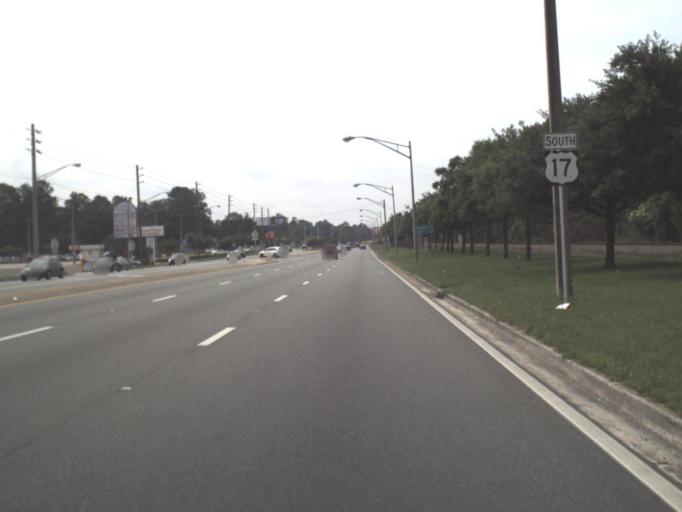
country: US
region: Florida
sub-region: Clay County
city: Orange Park
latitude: 30.2471
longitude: -81.6978
